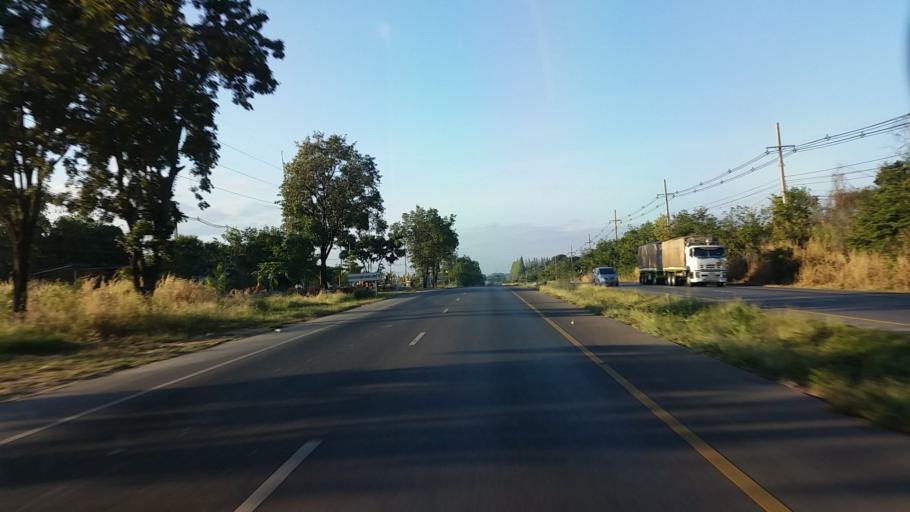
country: TH
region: Lop Buri
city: Chai Badan
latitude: 15.1956
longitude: 101.0826
